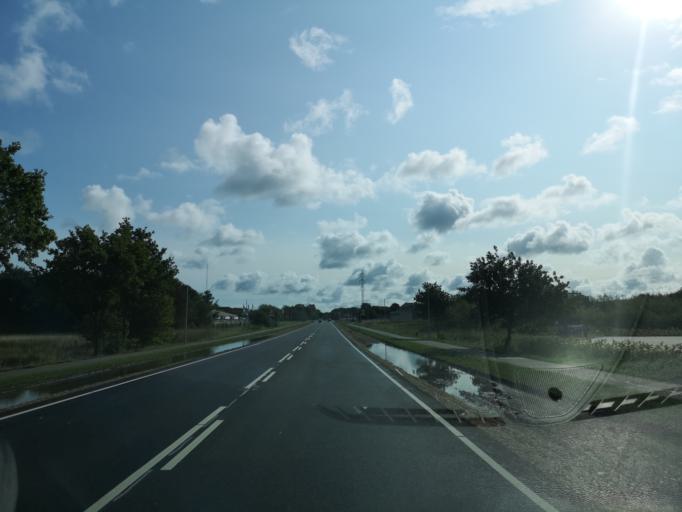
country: DK
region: Central Jutland
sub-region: Herning Kommune
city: Snejbjerg
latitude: 56.1347
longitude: 8.9247
